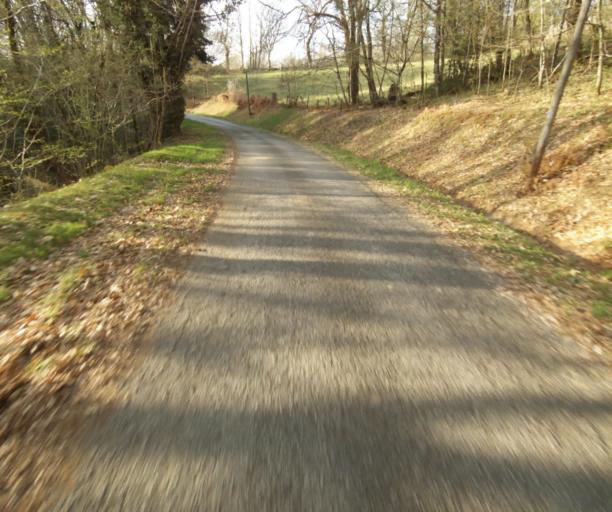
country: FR
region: Limousin
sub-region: Departement de la Correze
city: Correze
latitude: 45.3835
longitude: 1.8409
